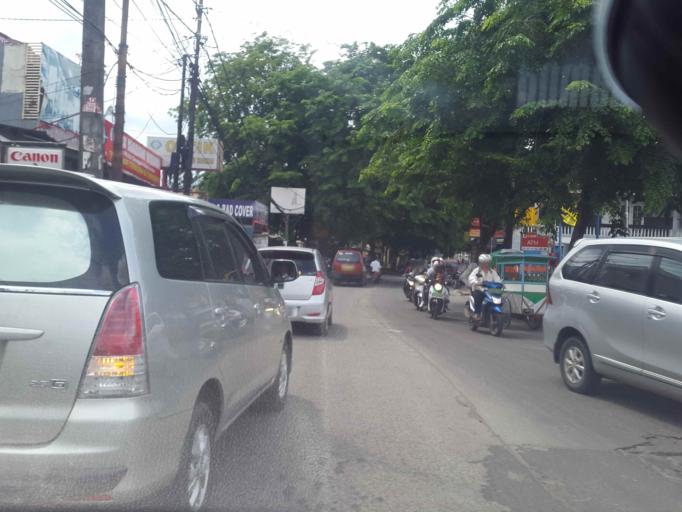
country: ID
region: West Java
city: Bekasi
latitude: -6.2948
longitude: 106.9653
